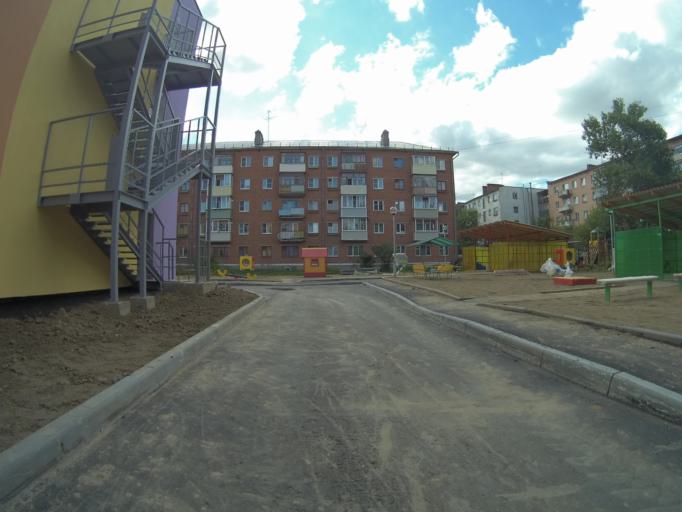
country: RU
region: Vladimir
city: Vladimir
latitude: 56.1195
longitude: 40.3697
